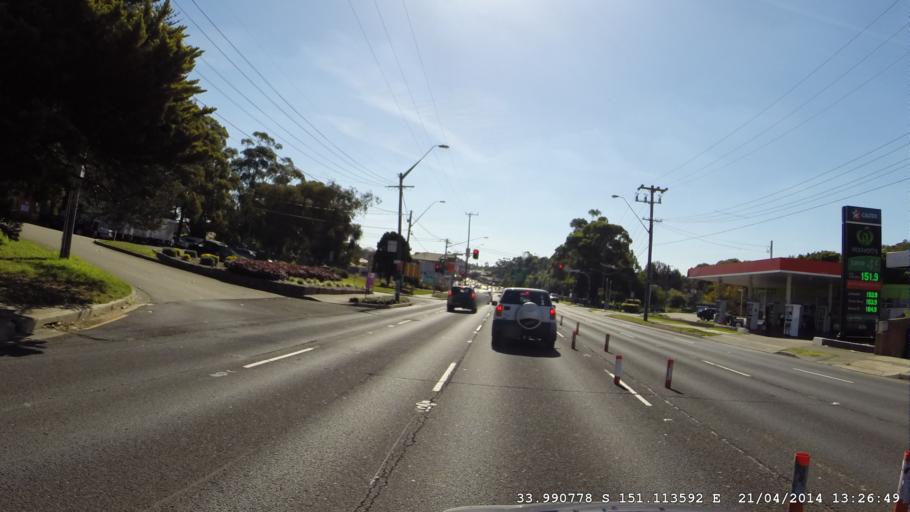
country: AU
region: New South Wales
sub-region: Kogarah
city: Blakehurst
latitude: -33.9908
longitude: 151.1136
